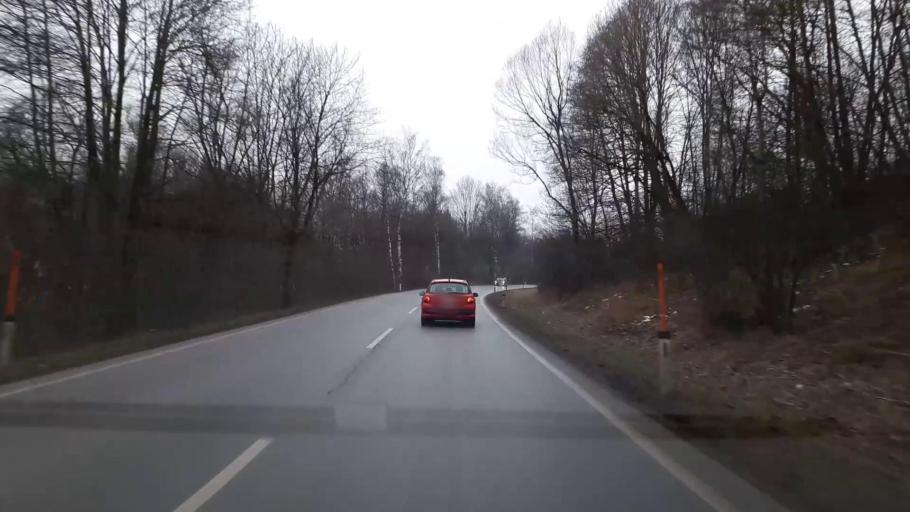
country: AT
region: Lower Austria
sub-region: Politischer Bezirk Neunkirchen
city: Thomasberg
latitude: 47.5650
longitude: 16.0972
